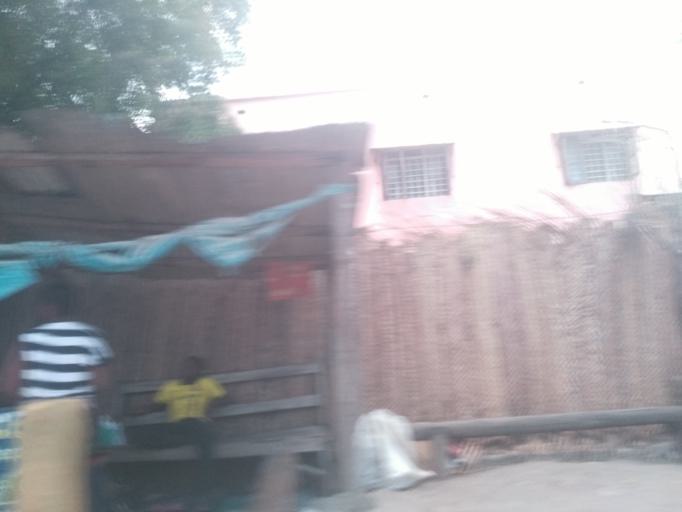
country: TZ
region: Dar es Salaam
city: Dar es Salaam
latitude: -6.8446
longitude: 39.2697
